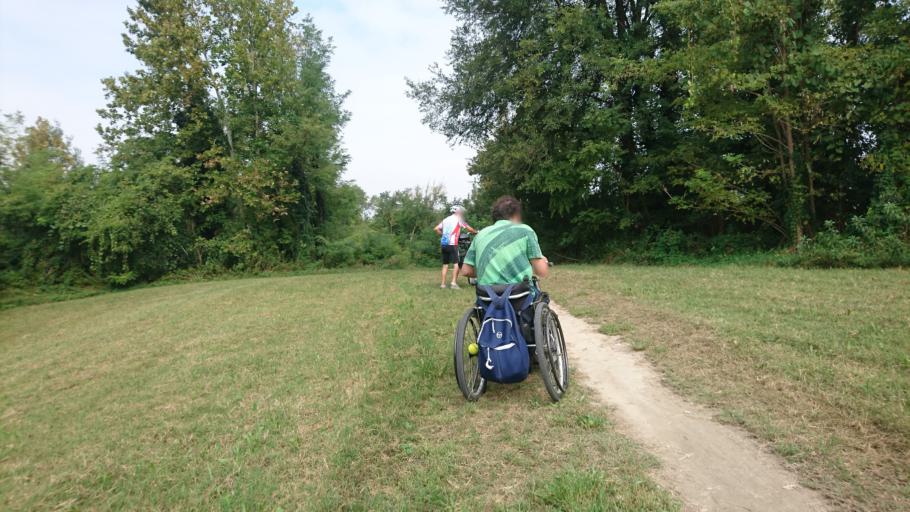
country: IT
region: Veneto
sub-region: Provincia di Padova
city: Piazzola sul Brenta
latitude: 45.5621
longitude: 11.7957
